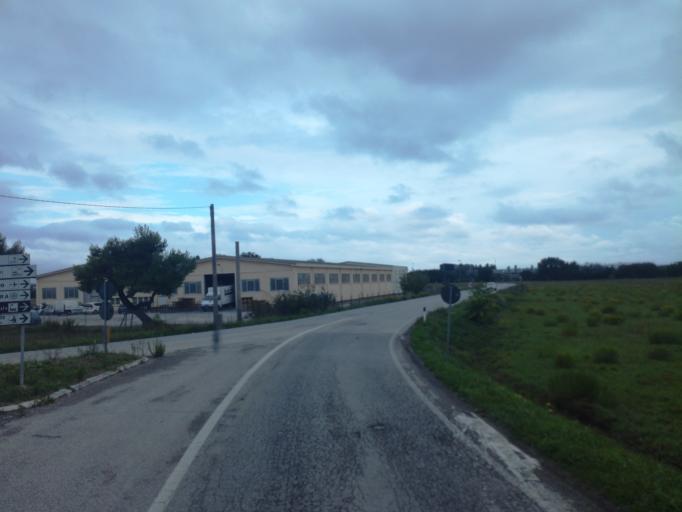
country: IT
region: The Marches
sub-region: Provincia di Ancona
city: Falconara Marittima
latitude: 43.6012
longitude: 13.3583
